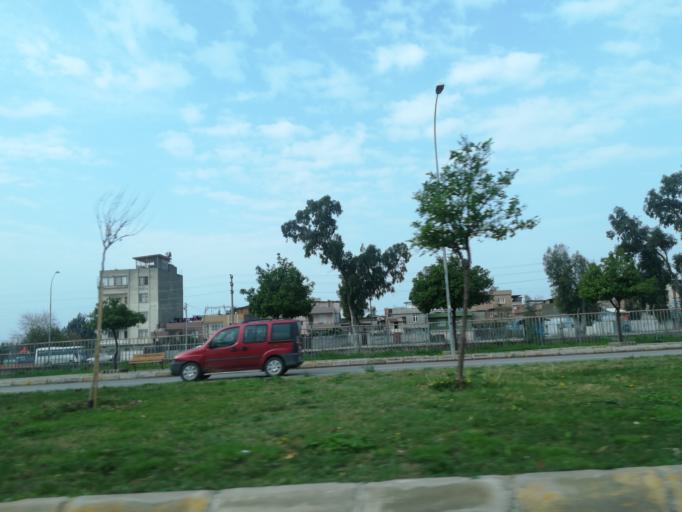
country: TR
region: Adana
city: Yuregir
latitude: 36.9939
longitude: 35.3606
